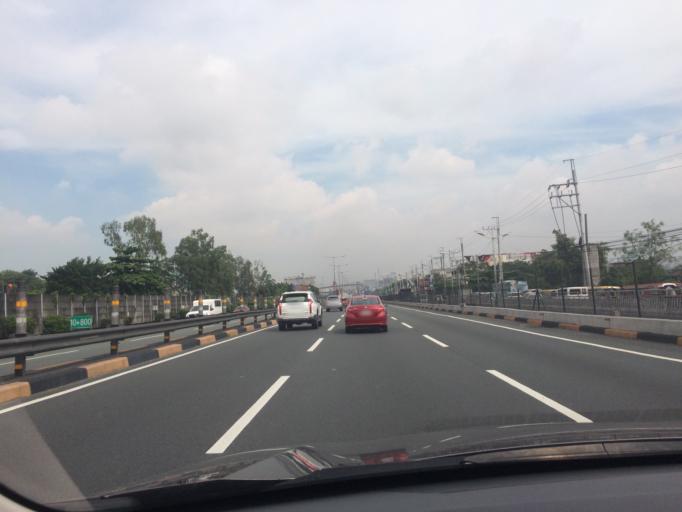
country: PH
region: Metro Manila
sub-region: Makati City
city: Makati City
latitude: 14.5152
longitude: 121.0311
